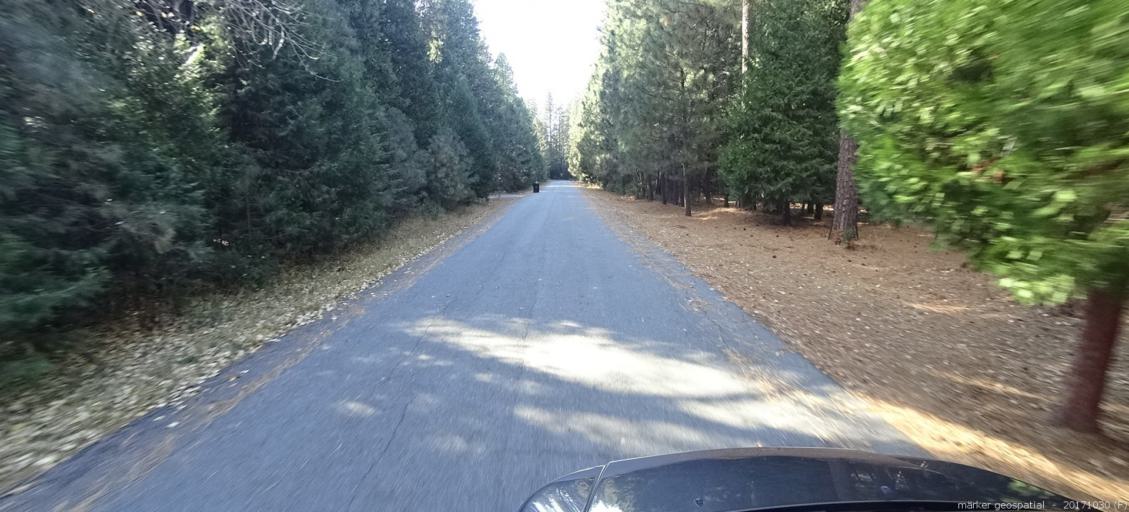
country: US
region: California
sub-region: Shasta County
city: Shingletown
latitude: 40.5232
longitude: -121.6861
